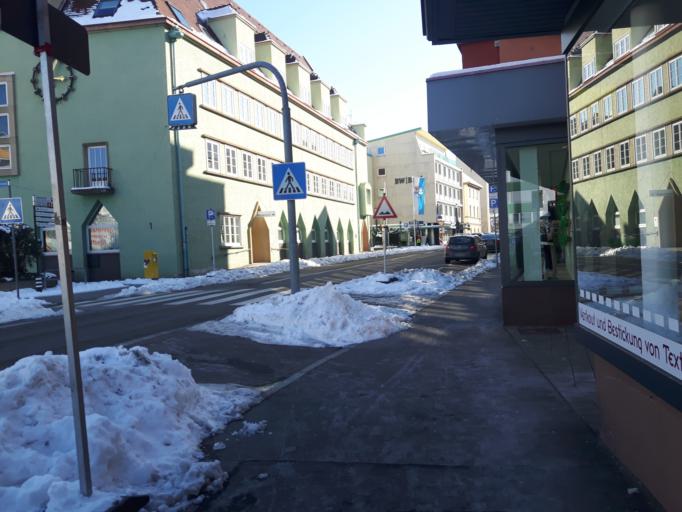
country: DE
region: Baden-Wuerttemberg
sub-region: Freiburg Region
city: Dauchingen
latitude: 48.0659
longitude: 8.5356
